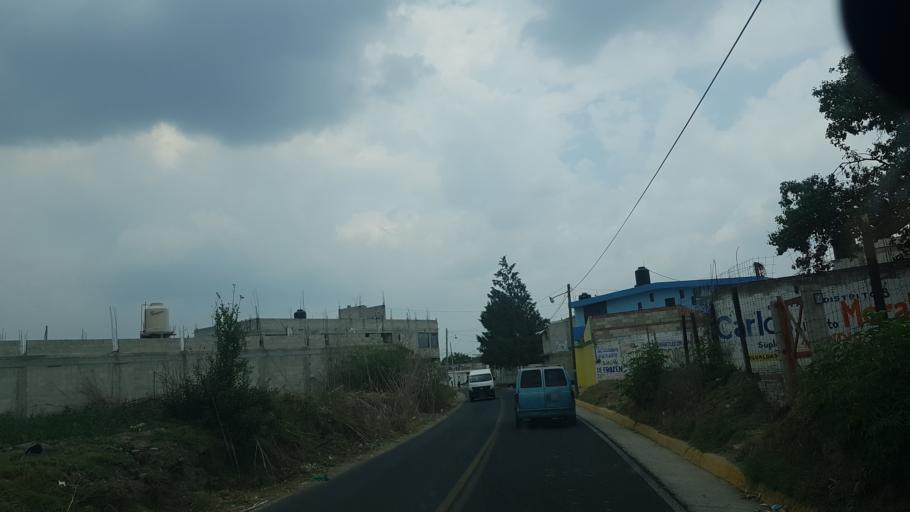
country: MX
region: Puebla
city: Huejotzingo
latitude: 19.1587
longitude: -98.4187
